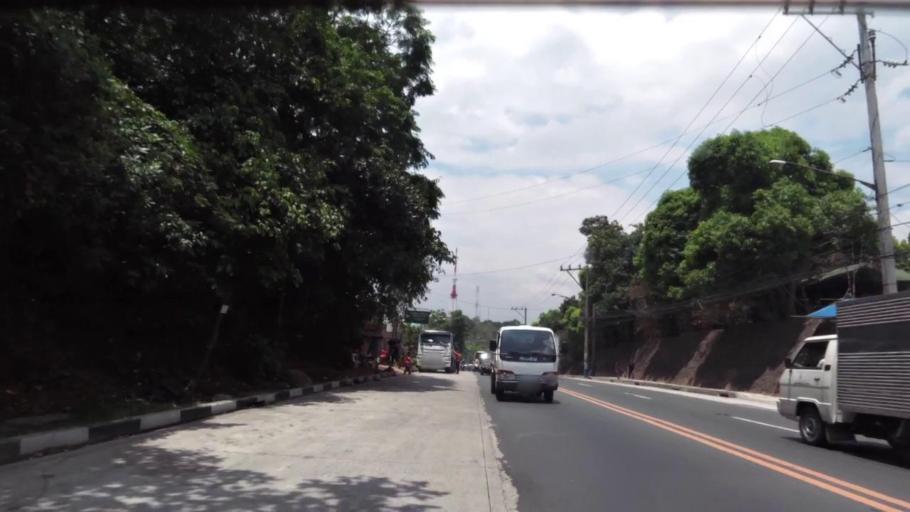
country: PH
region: Calabarzon
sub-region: Province of Rizal
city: Antipolo
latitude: 14.6070
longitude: 121.1697
